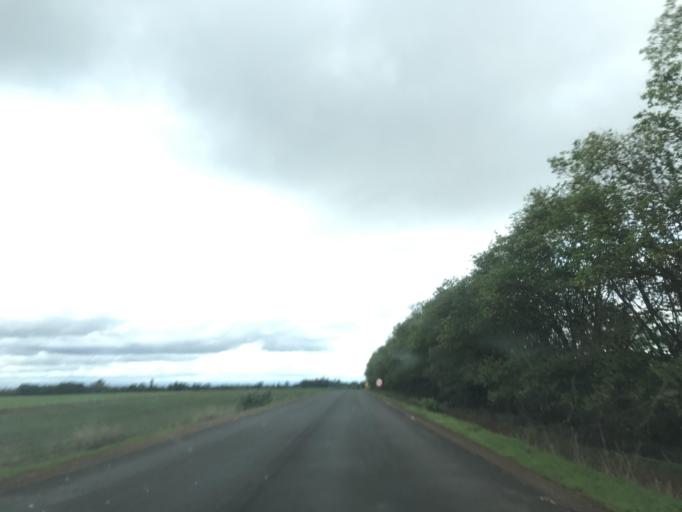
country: BR
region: Goias
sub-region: Vianopolis
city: Vianopolis
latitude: -16.7912
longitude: -48.5214
